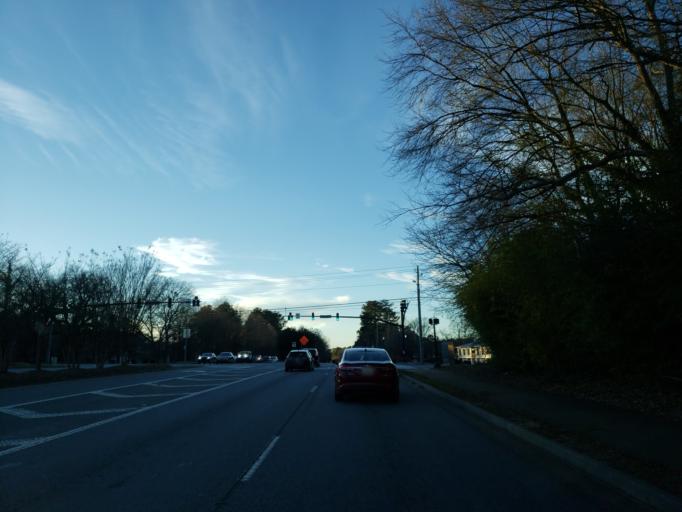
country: US
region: Georgia
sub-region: Fulton County
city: Alpharetta
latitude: 34.0715
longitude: -84.2979
